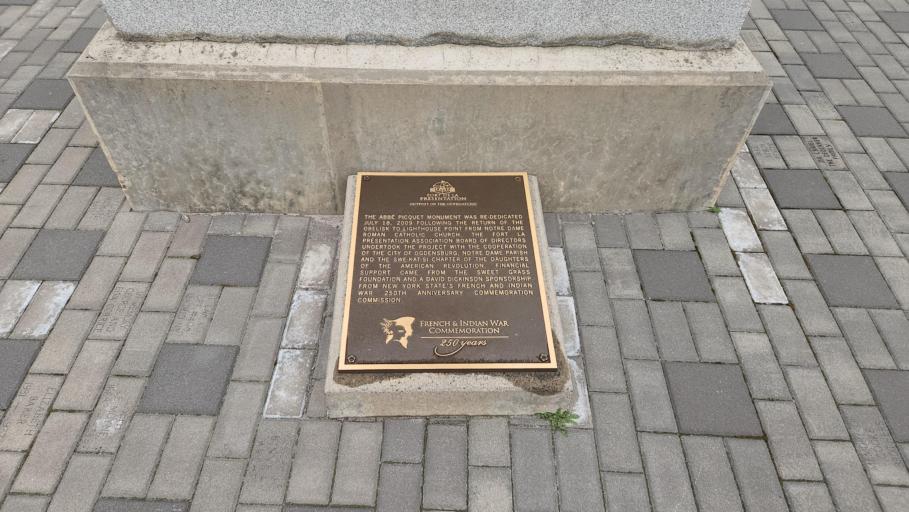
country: US
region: New York
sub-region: St. Lawrence County
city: Ogdensburg
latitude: 44.6945
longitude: -75.5013
